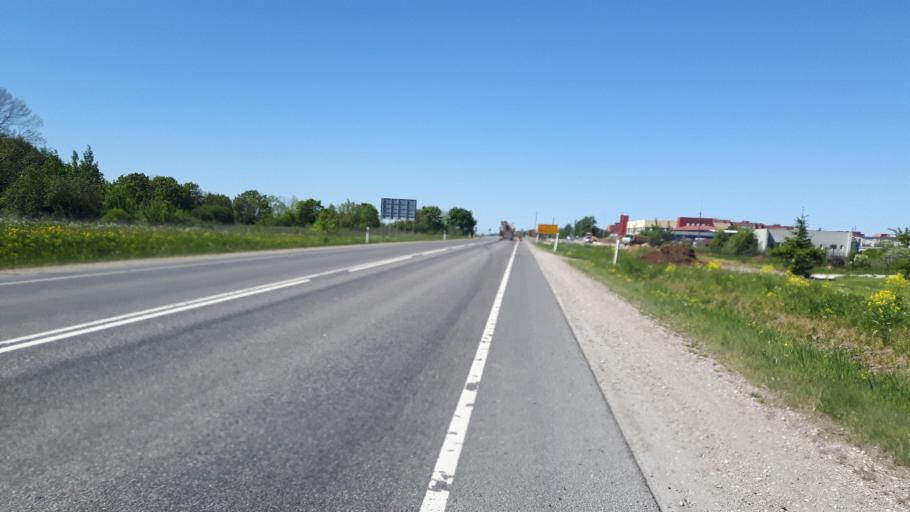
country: EE
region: Ida-Virumaa
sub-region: Sillamaee linn
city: Sillamae
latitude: 59.3878
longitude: 27.8072
